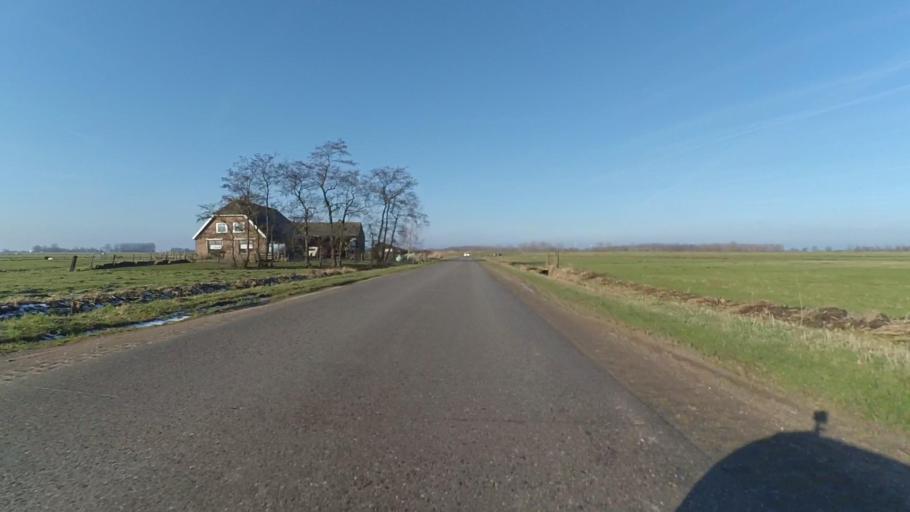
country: NL
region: Gelderland
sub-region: Gemeente Nijkerk
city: Nijkerk
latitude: 52.2612
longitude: 5.4926
